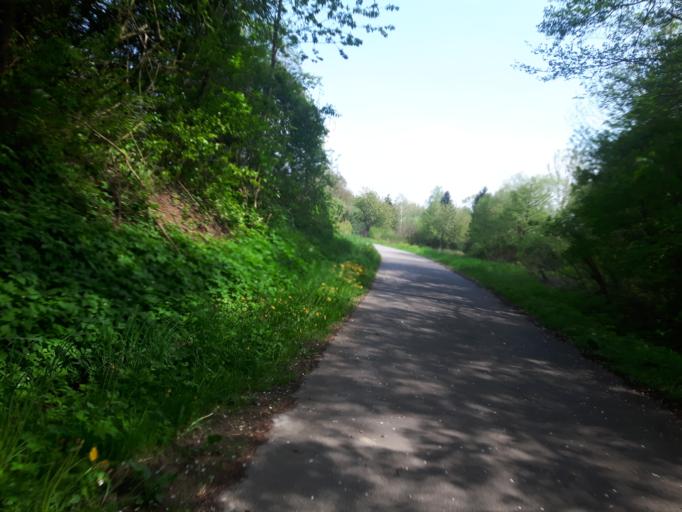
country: DE
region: Baden-Wuerttemberg
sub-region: Karlsruhe Region
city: Muhlhausen
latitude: 49.2478
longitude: 8.7470
